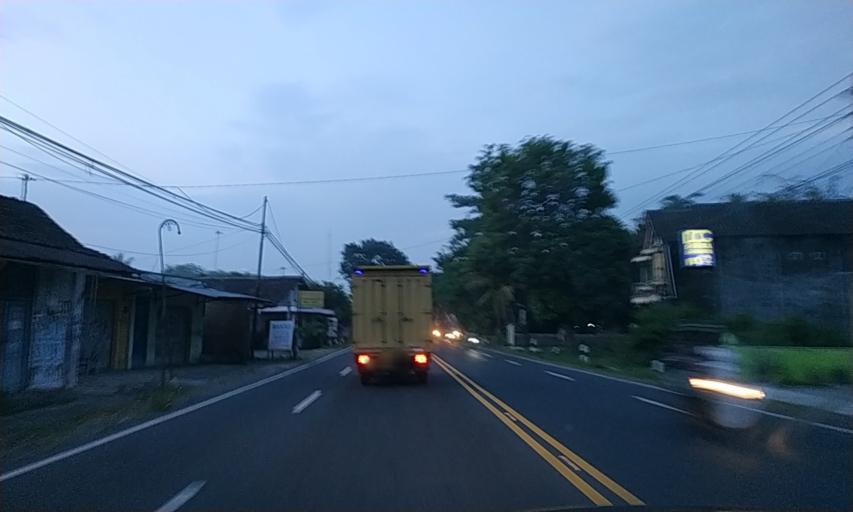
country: ID
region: Daerah Istimewa Yogyakarta
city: Godean
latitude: -7.8370
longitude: 110.2199
